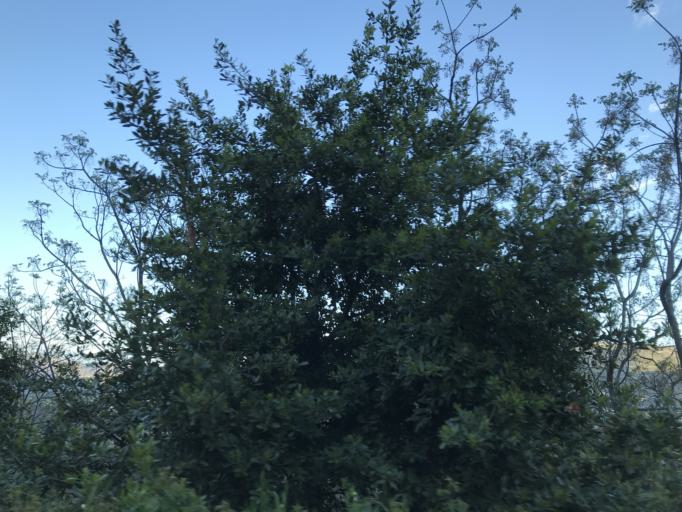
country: TR
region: Hatay
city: Buyukcat
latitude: 36.1007
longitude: 36.0545
